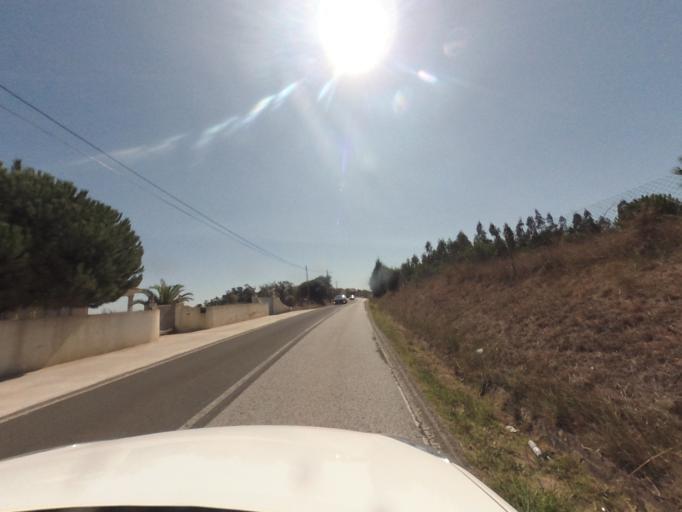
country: PT
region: Leiria
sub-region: Alcobaca
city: Turquel
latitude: 39.5001
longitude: -8.9759
